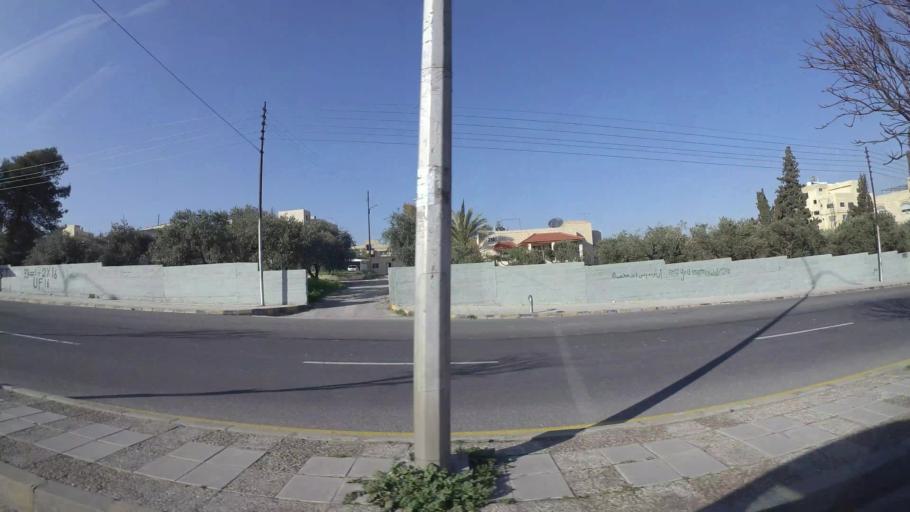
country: JO
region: Amman
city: Amman
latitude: 31.9741
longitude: 35.9665
